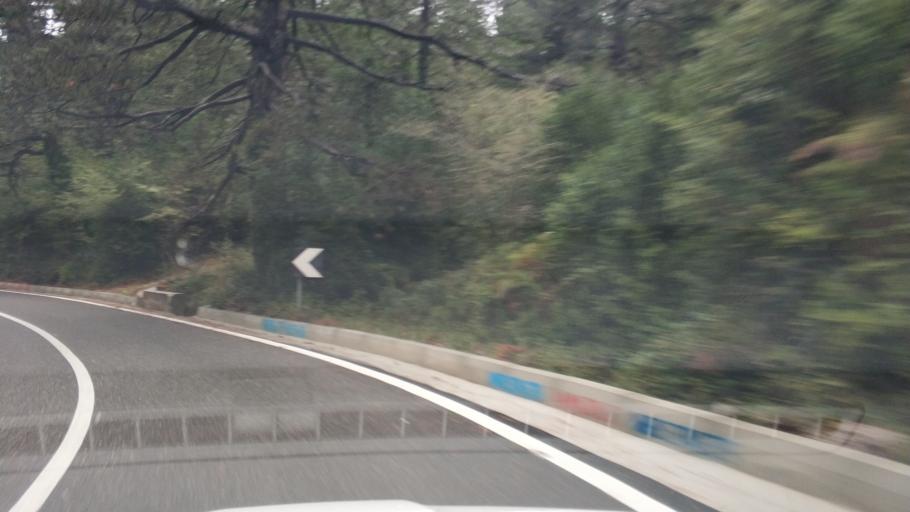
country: AL
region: Vlore
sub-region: Rrethi i Vlores
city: Brataj
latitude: 40.2066
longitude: 19.5853
